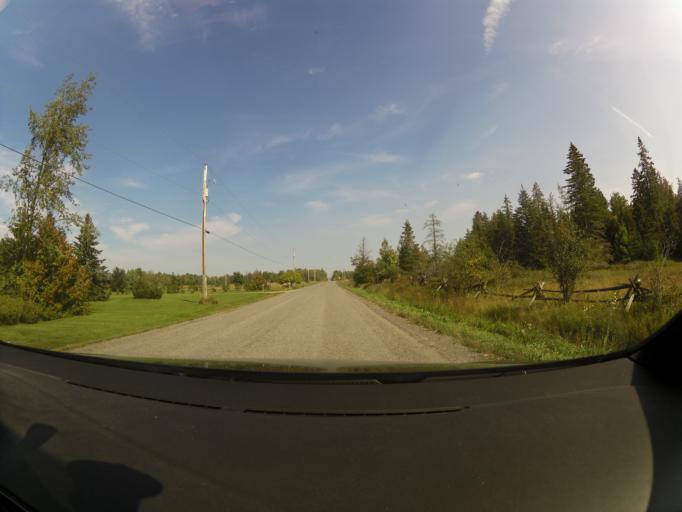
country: CA
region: Ontario
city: Carleton Place
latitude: 45.2992
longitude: -76.2172
